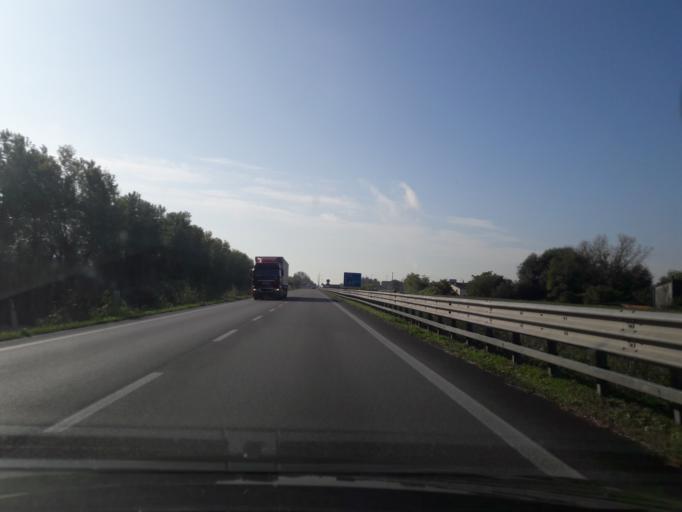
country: IT
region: Veneto
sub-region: Provincia di Venezia
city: Campagna Lupia
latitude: 45.3702
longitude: 12.1380
